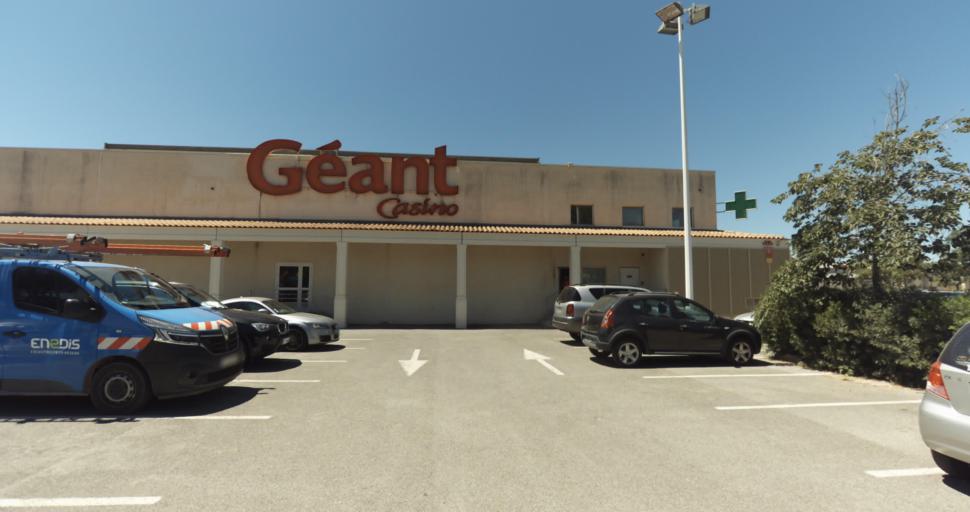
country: FR
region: Provence-Alpes-Cote d'Azur
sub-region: Departement du Var
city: Gassin
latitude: 43.2628
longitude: 6.5810
